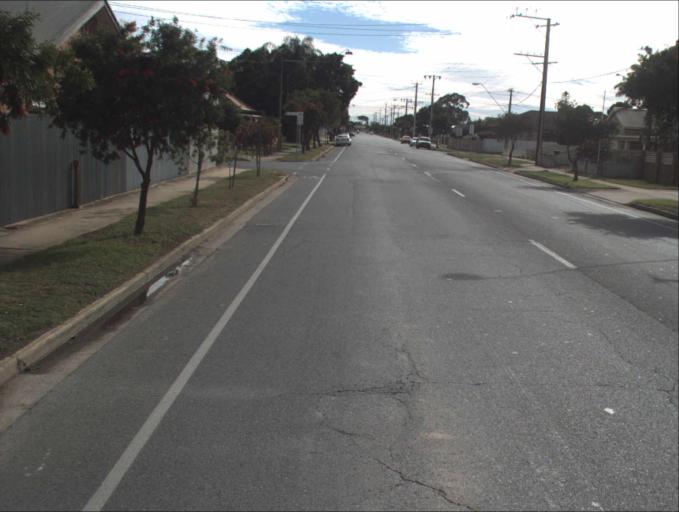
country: AU
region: South Australia
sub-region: Port Adelaide Enfield
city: Alberton
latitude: -34.8592
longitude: 138.5292
